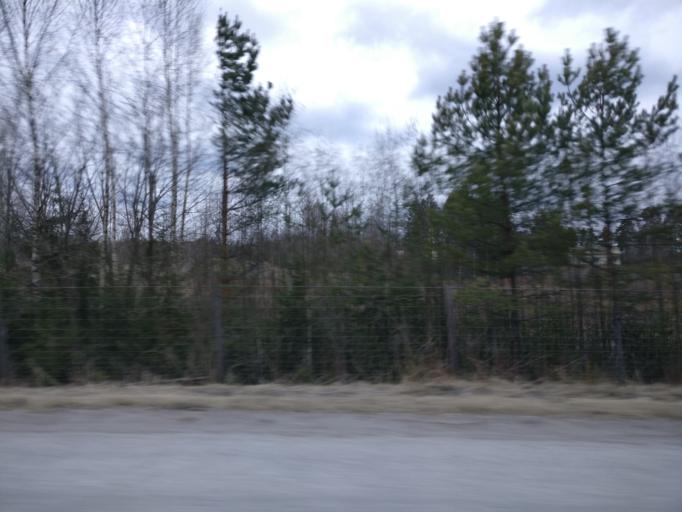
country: FI
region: Haeme
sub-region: Riihimaeki
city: Riihimaeki
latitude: 60.7090
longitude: 24.7365
